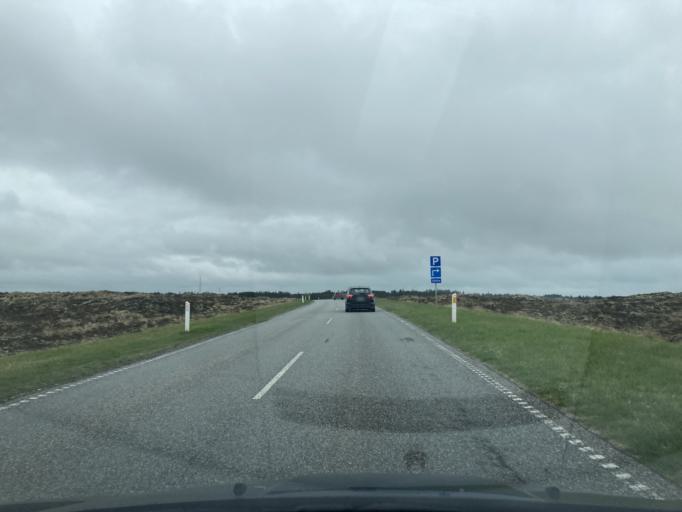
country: DK
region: North Denmark
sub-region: Thisted Kommune
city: Hurup
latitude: 56.9574
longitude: 8.4006
